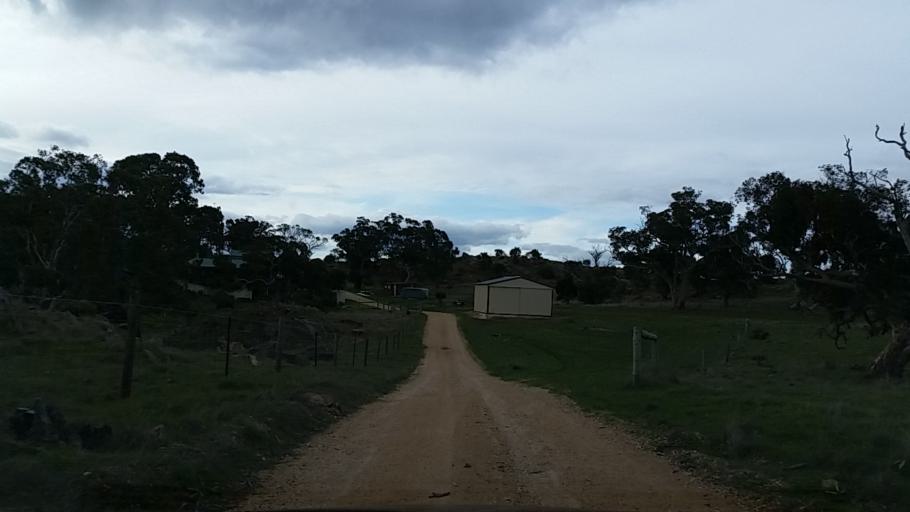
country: AU
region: South Australia
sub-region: Mount Barker
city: Callington
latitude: -34.9562
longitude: 139.0577
